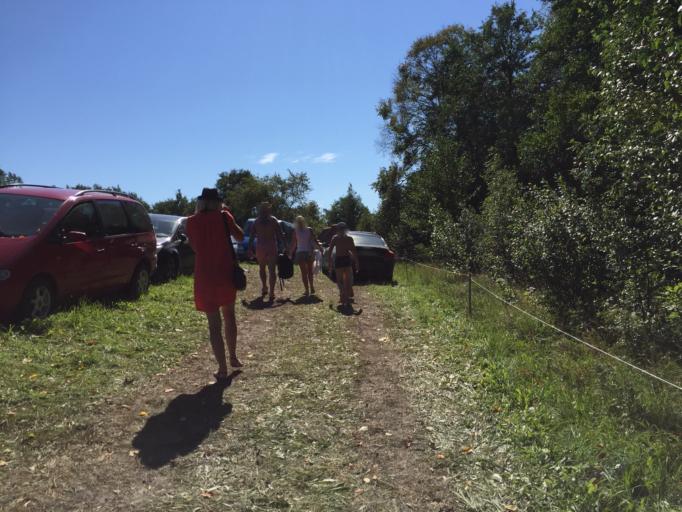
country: LT
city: Zarasai
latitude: 55.7864
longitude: 25.9613
